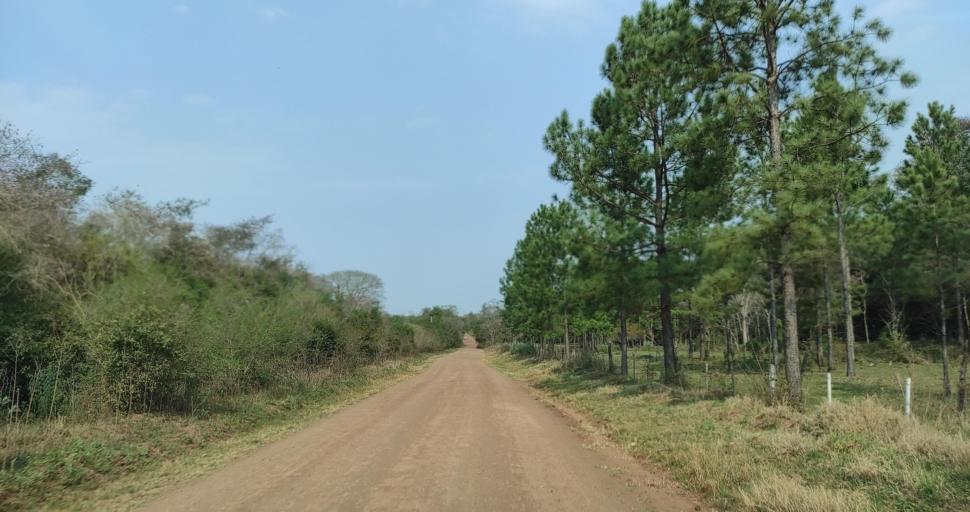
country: AR
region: Misiones
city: Cerro Cora
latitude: -27.5178
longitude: -55.6022
